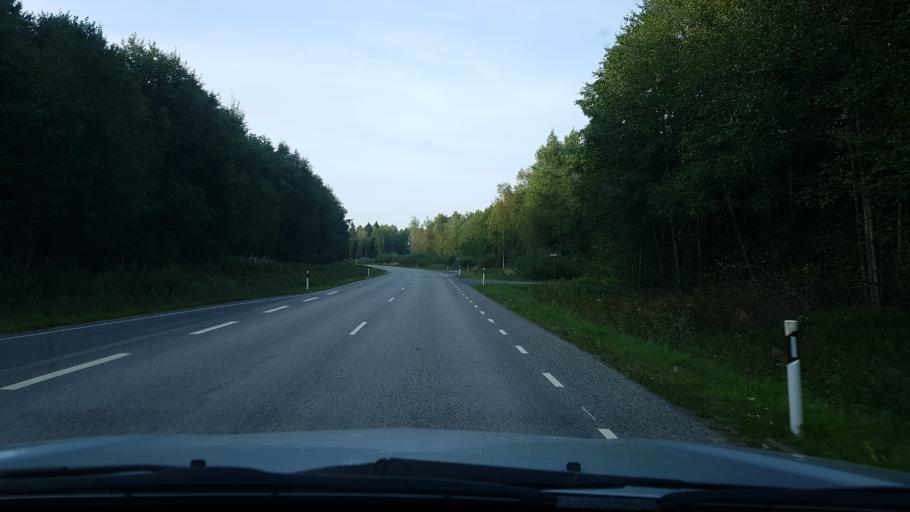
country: EE
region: Ida-Virumaa
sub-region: Narva-Joesuu linn
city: Narva-Joesuu
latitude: 59.3432
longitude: 27.9329
